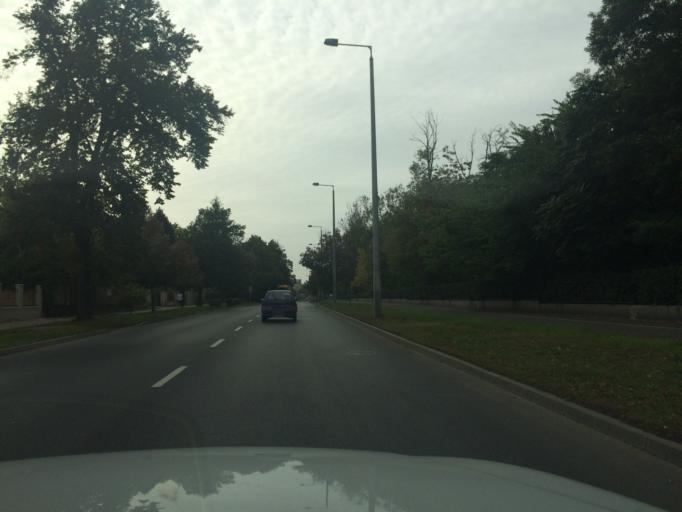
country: HU
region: Szabolcs-Szatmar-Bereg
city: Nyiregyhaza
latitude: 47.9736
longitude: 21.7165
